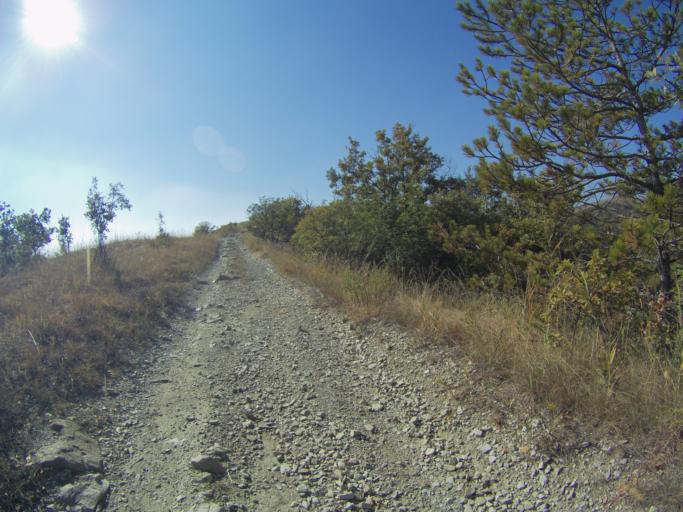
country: IT
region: Emilia-Romagna
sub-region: Provincia di Reggio Emilia
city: Quattro Castella
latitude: 44.5880
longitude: 10.4873
